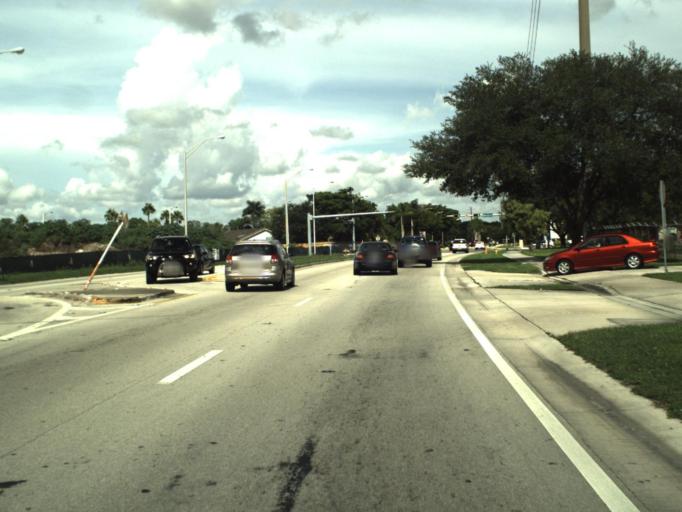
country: US
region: Florida
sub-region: Miami-Dade County
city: Country Club
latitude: 25.9399
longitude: -80.2981
